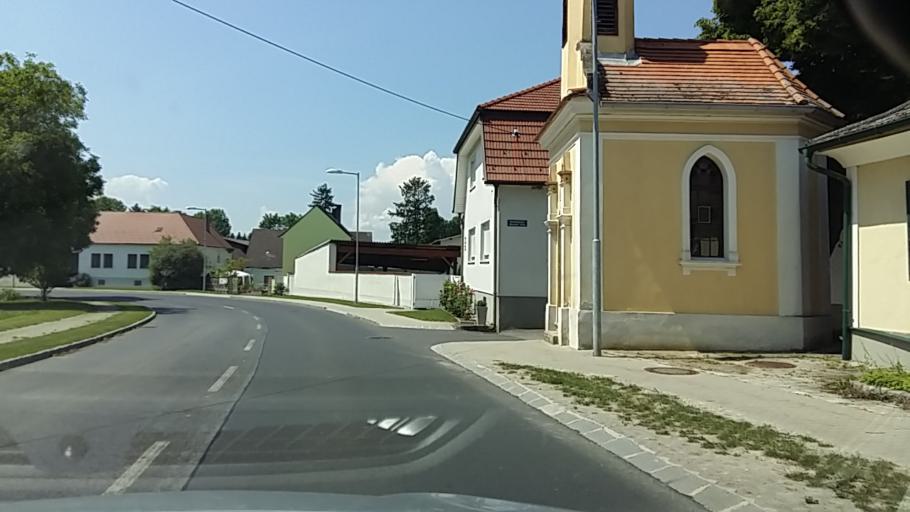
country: AT
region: Burgenland
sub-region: Politischer Bezirk Oberpullendorf
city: Raiding
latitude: 47.5444
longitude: 16.5531
